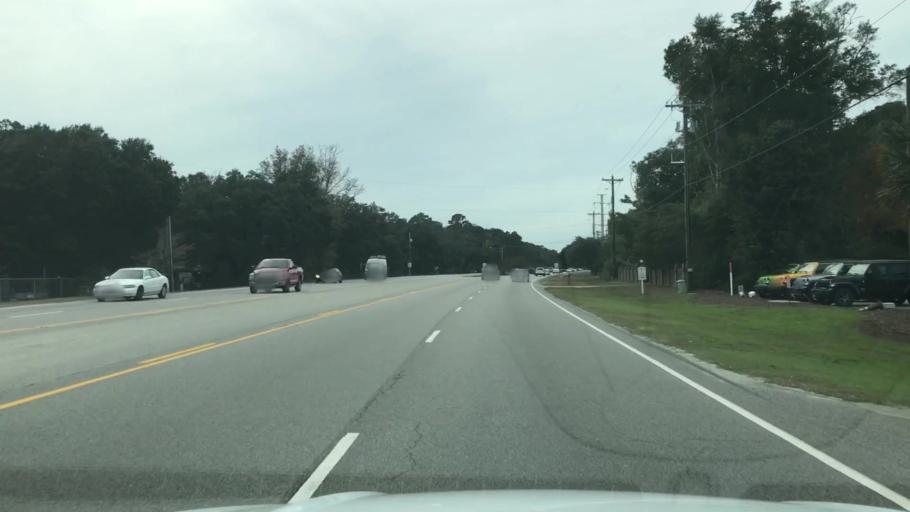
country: US
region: South Carolina
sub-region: Georgetown County
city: Georgetown
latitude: 33.4282
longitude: -79.1500
